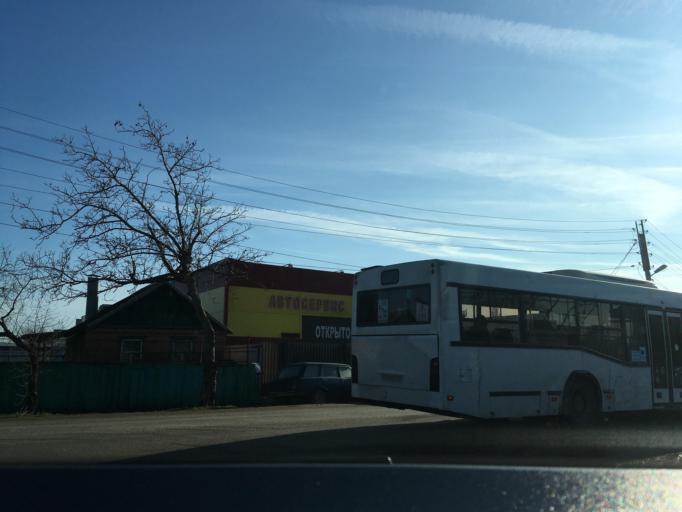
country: RU
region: Krasnodarskiy
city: Krasnodar
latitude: 45.1259
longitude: 39.0109
